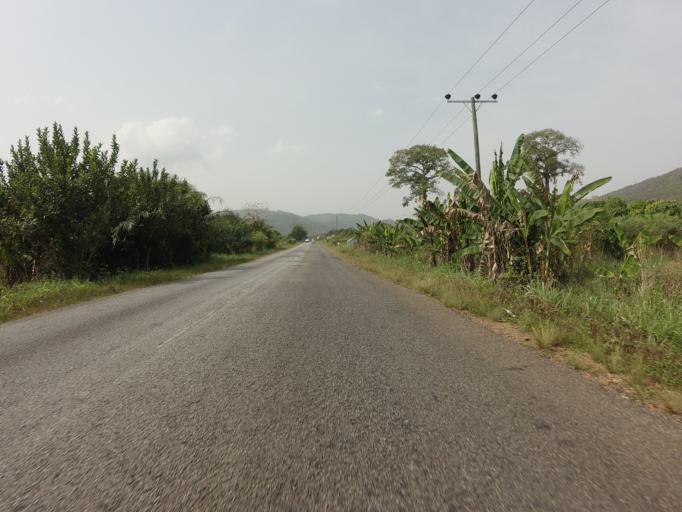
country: GH
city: Akropong
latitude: 6.3025
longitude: 0.1395
